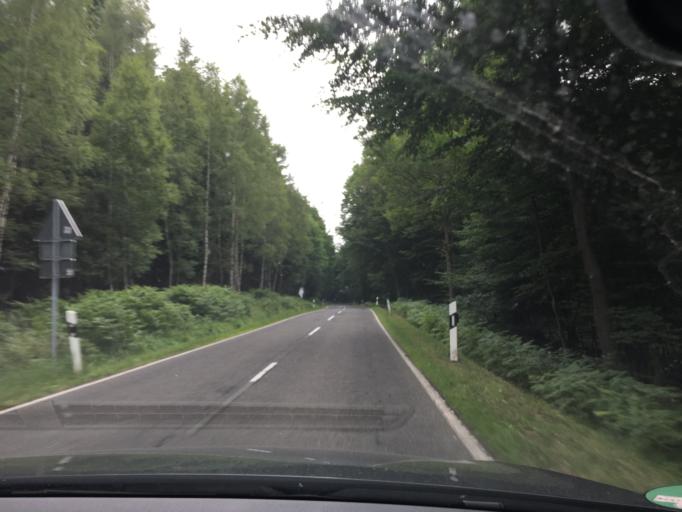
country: DE
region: North Rhine-Westphalia
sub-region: Regierungsbezirk Koln
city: Langerwehe
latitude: 50.7721
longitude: 6.3810
